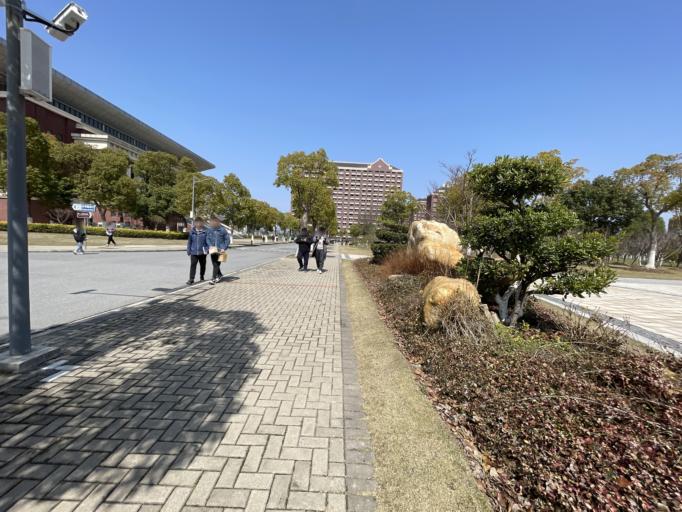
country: CN
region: Shanghai Shi
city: Shuyuan
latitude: 30.8942
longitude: 121.8851
